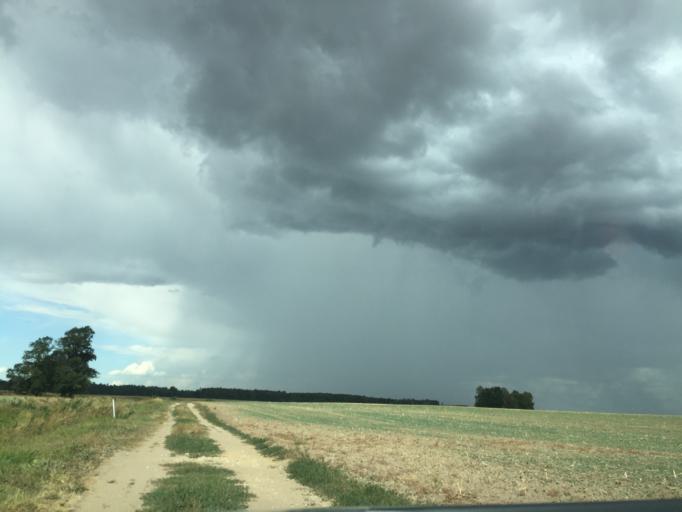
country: LT
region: Siauliu apskritis
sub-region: Joniskis
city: Joniskis
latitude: 56.2893
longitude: 23.7266
